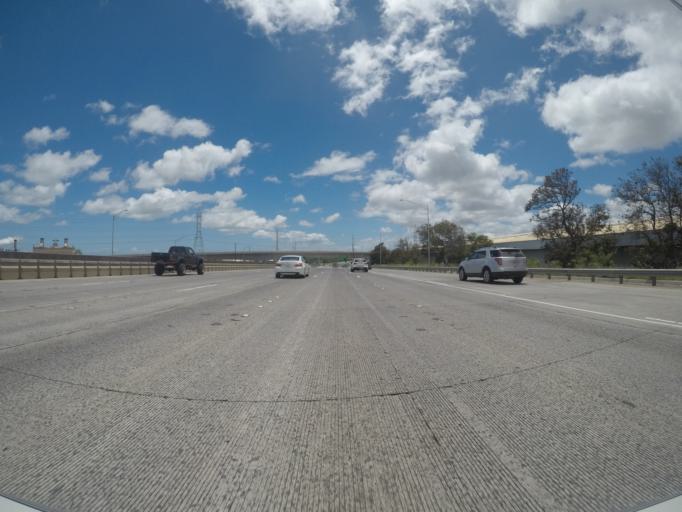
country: US
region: Hawaii
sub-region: Honolulu County
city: Pearl City, Manana
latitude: 21.3919
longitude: -157.9607
